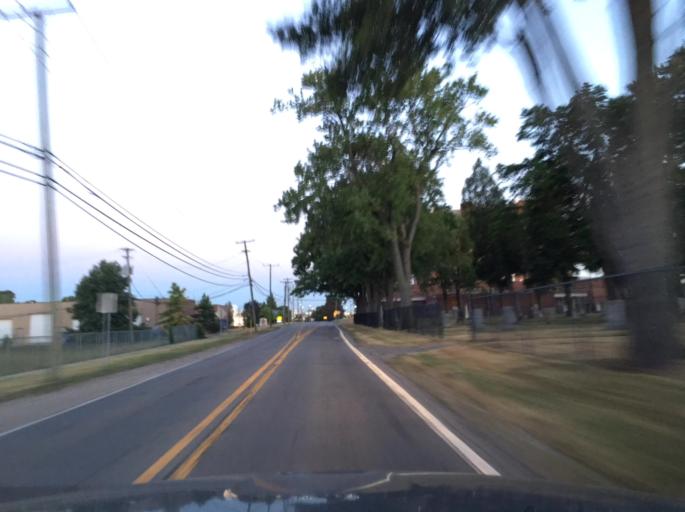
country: US
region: Michigan
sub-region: Macomb County
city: Mount Clemens
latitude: 42.6191
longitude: -82.8879
